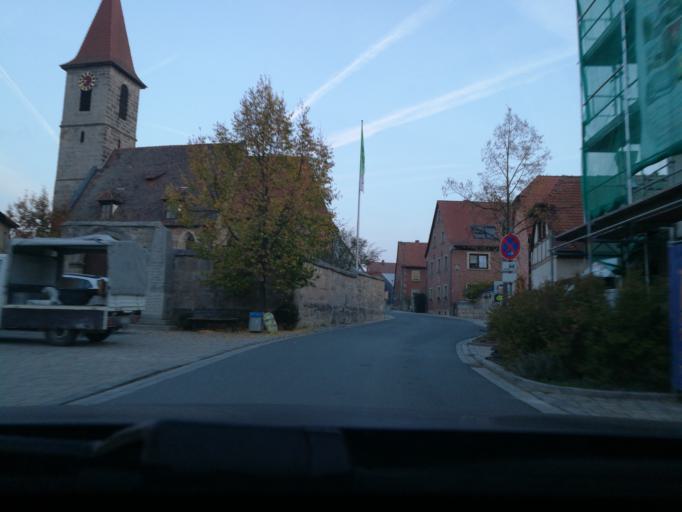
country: DE
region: Bavaria
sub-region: Regierungsbezirk Mittelfranken
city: Seukendorf
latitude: 49.4865
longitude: 10.8787
